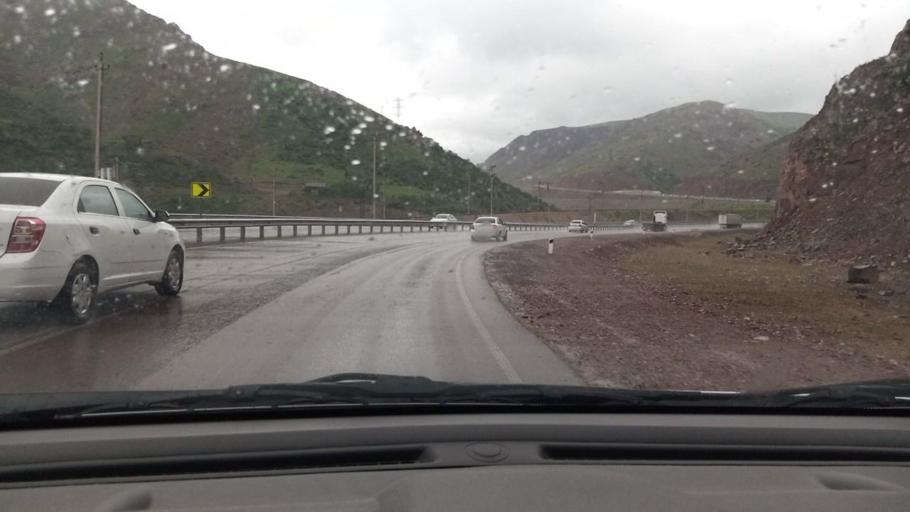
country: UZ
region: Toshkent
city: Angren
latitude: 41.0739
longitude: 70.3112
